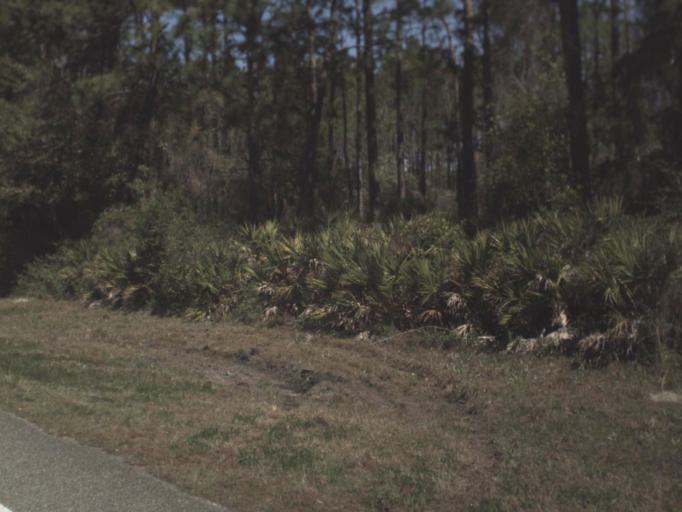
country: US
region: Florida
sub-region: Gulf County
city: Port Saint Joe
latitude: 29.7586
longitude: -85.2574
